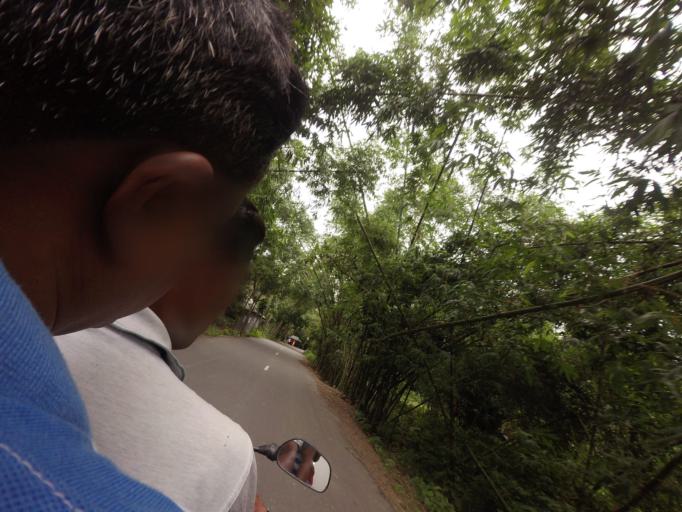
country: BD
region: Khulna
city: Kalia
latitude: 23.1634
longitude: 89.6444
